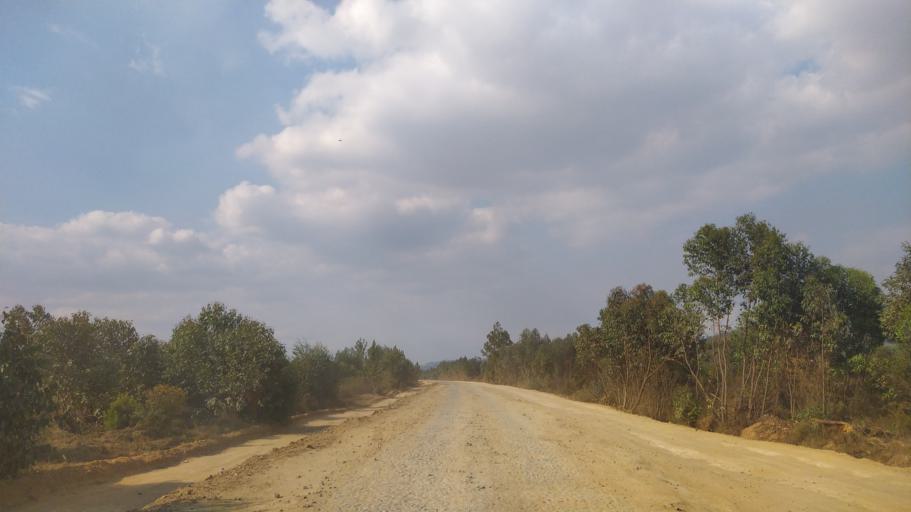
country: MG
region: Alaotra Mangoro
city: Moramanga
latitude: -18.6478
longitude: 48.2746
